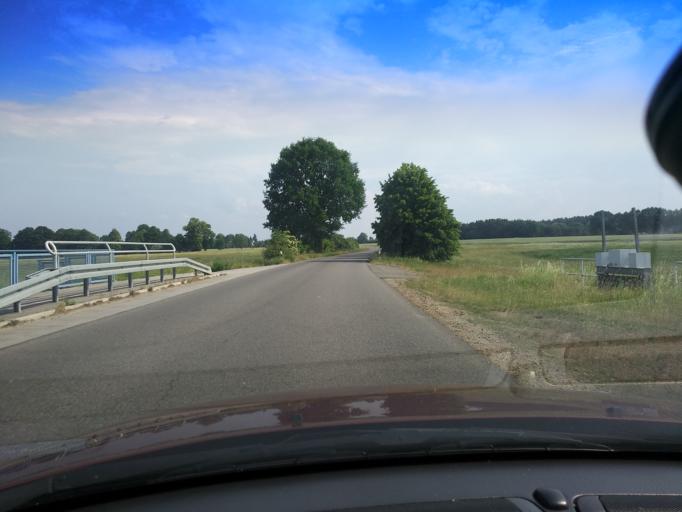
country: DE
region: Saxony
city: Klitten
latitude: 51.3552
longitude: 14.5850
